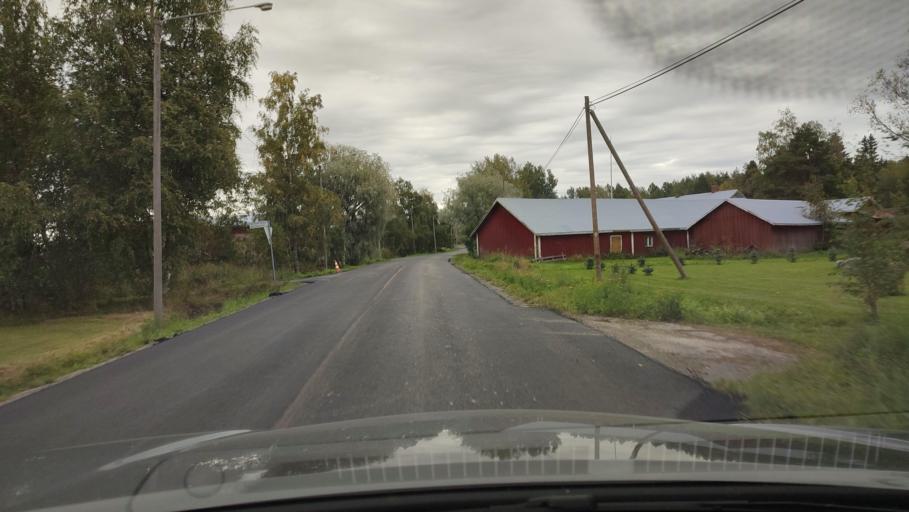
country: FI
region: Ostrobothnia
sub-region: Sydosterbotten
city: Kristinestad
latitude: 62.2498
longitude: 21.5252
